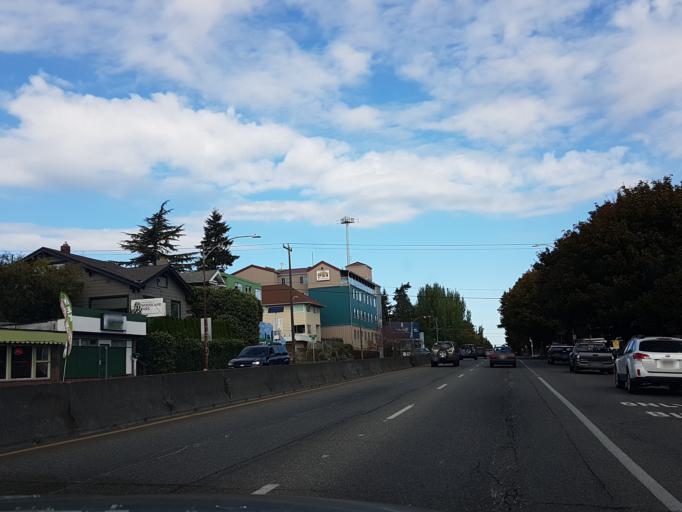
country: US
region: Washington
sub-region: King County
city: Seattle
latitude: 47.6629
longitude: -122.3473
